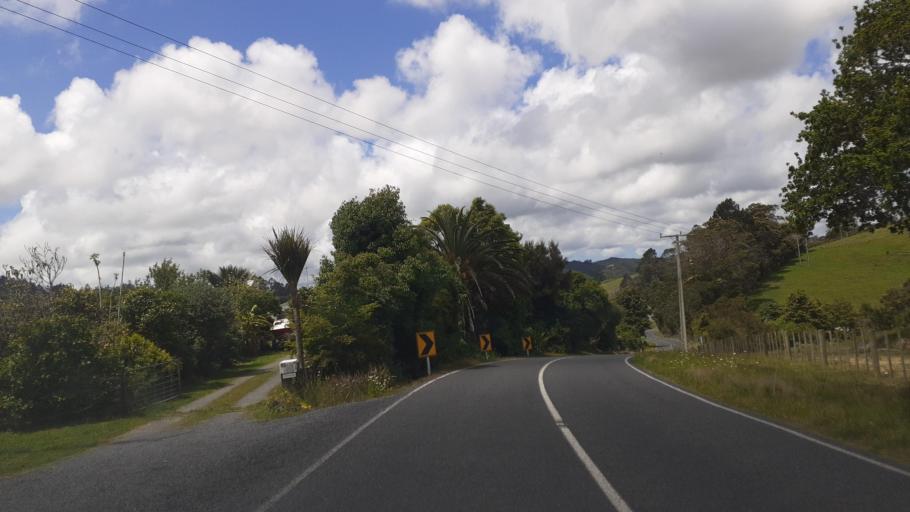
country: NZ
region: Northland
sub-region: Far North District
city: Kawakawa
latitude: -35.3629
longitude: 174.0960
